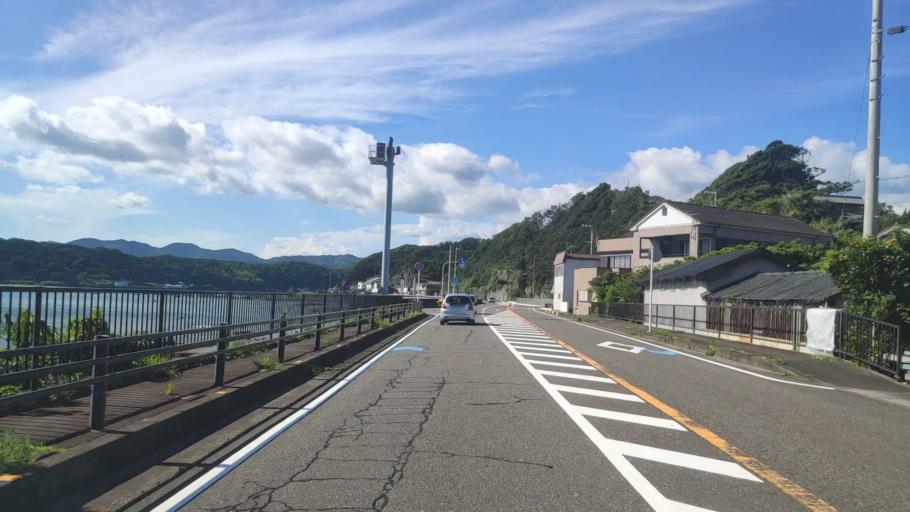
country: JP
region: Wakayama
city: Shingu
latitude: 33.4694
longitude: 135.7748
